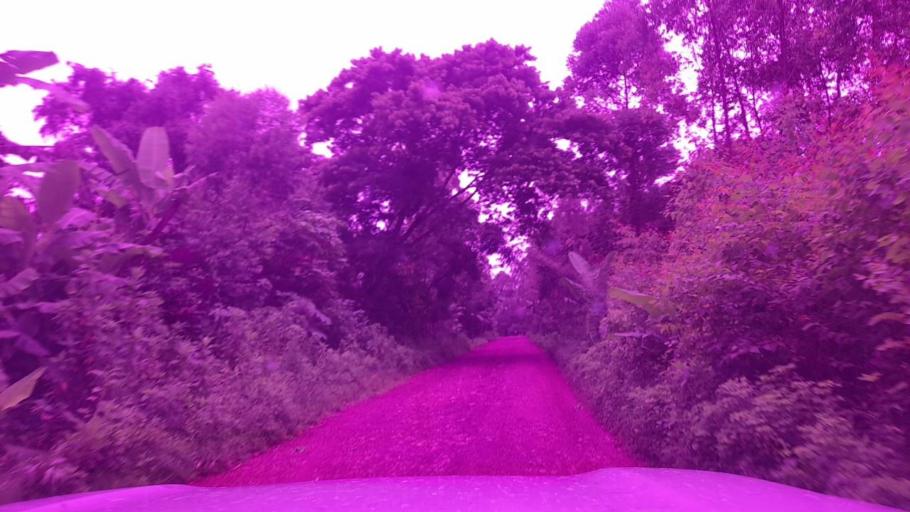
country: ET
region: Southern Nations, Nationalities, and People's Region
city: Bonga
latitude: 7.5772
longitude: 36.0239
